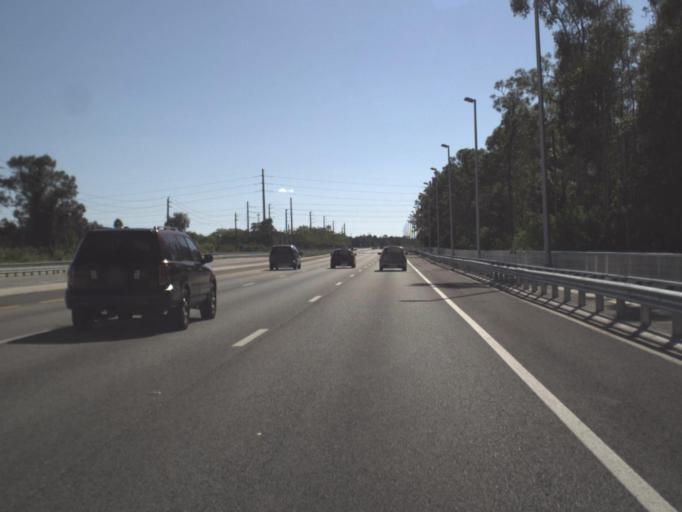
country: US
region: Florida
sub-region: Lee County
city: Tice
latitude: 26.6301
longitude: -81.7875
